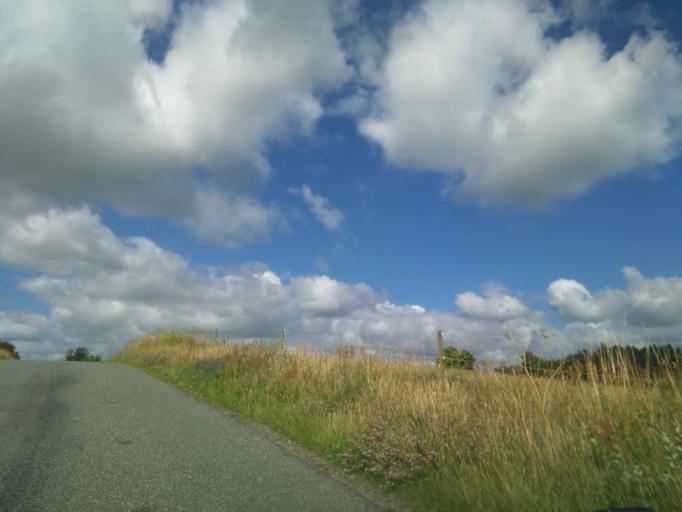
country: DK
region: Central Jutland
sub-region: Syddjurs Kommune
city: Ronde
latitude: 56.2278
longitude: 10.5200
